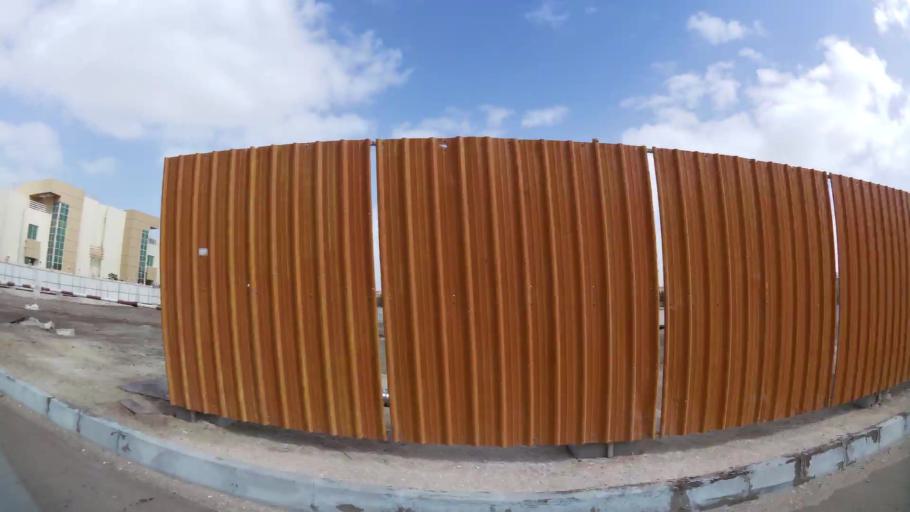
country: AE
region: Abu Dhabi
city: Abu Dhabi
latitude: 24.4103
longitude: 54.4946
